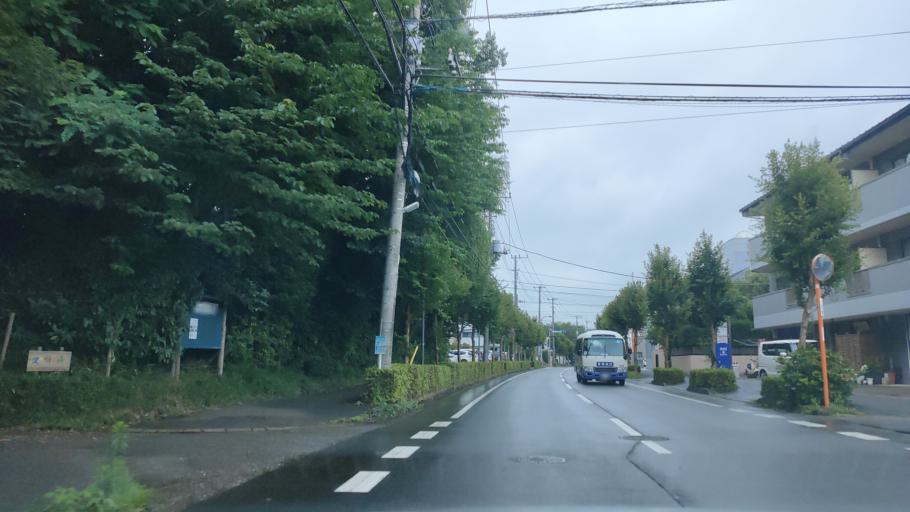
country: JP
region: Chiba
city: Nagareyama
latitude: 35.8773
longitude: 139.9164
